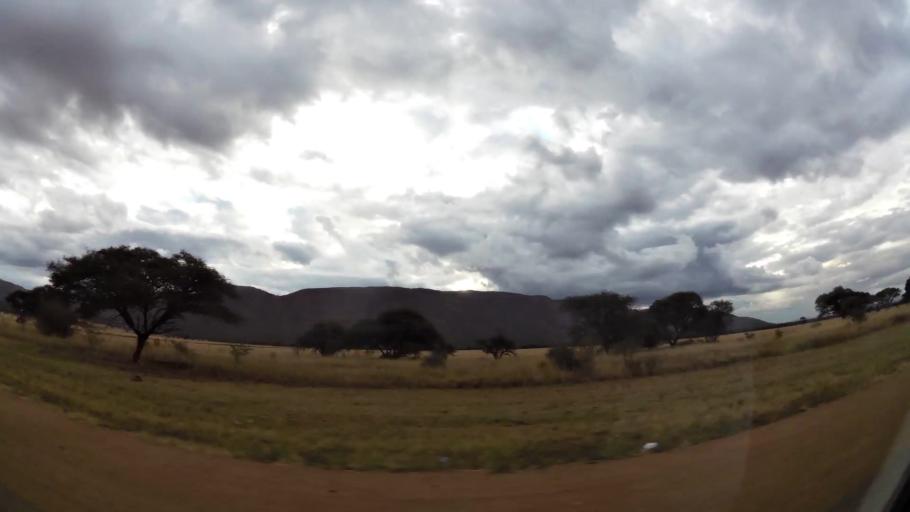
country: ZA
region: Limpopo
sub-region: Waterberg District Municipality
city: Mokopane
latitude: -24.2511
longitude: 28.9902
